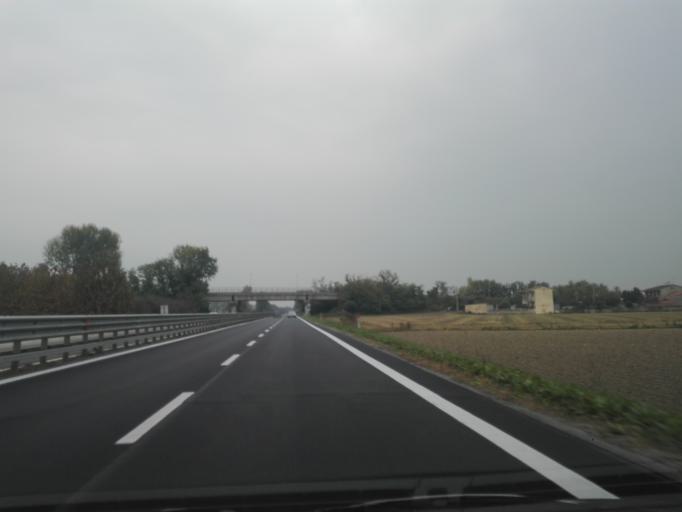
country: IT
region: Veneto
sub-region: Provincia di Verona
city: Villa Bartolomea
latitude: 45.1593
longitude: 11.3143
